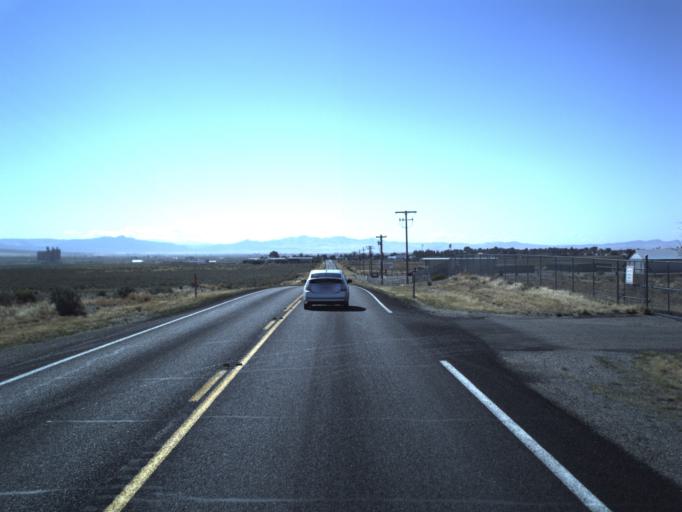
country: US
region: Utah
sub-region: Beaver County
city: Milford
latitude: 38.4186
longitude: -113.0099
